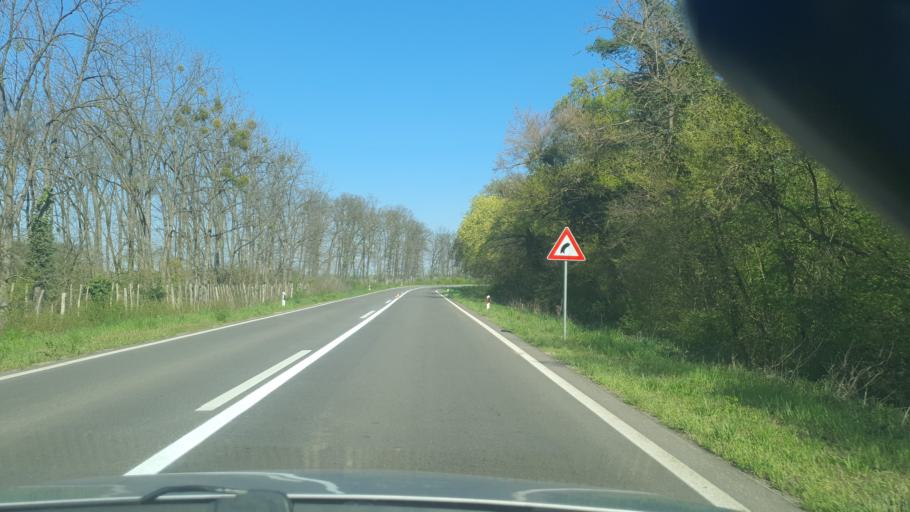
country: RS
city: Gakovo
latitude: 45.8317
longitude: 19.0122
